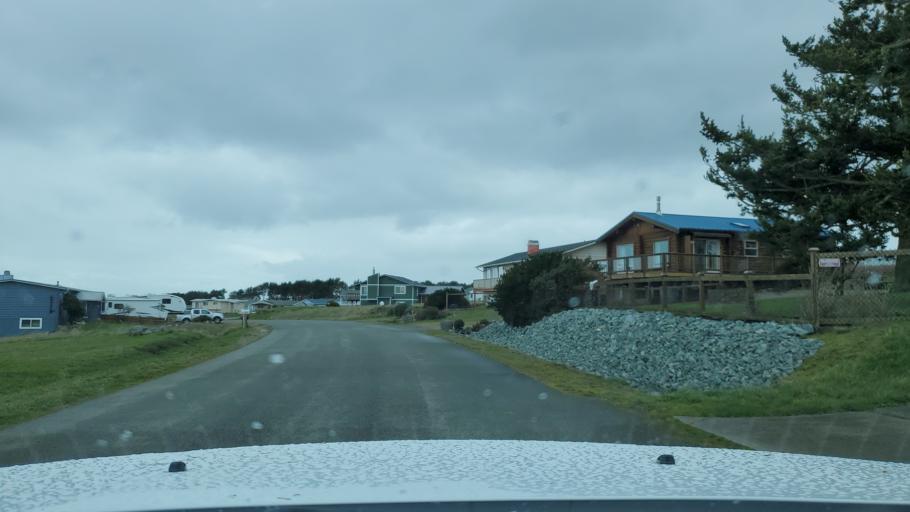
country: US
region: Washington
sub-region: Island County
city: Coupeville
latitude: 48.2367
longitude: -122.7586
